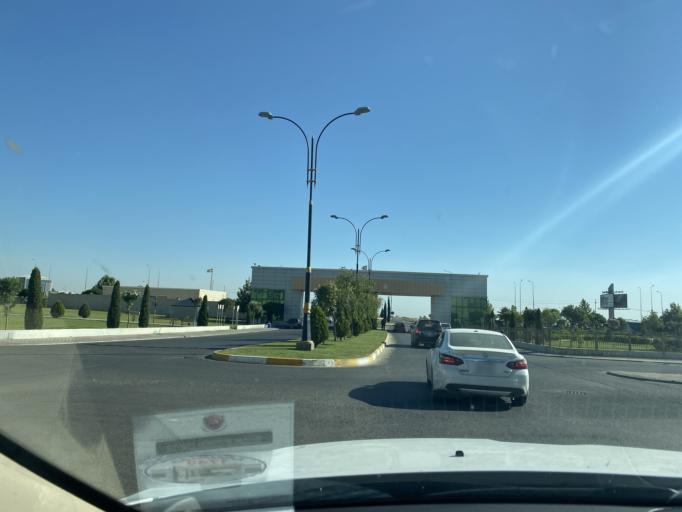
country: IQ
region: Arbil
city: Erbil
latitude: 36.2396
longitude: 44.0495
